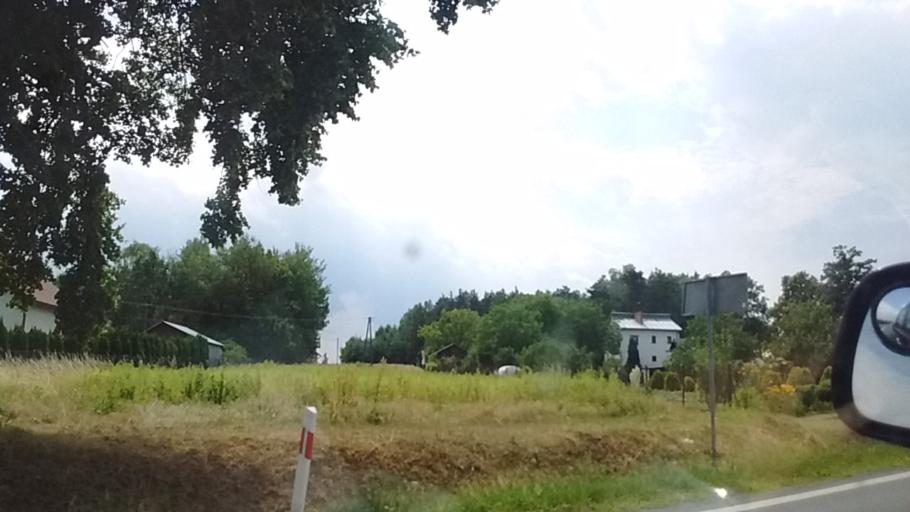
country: PL
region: Subcarpathian Voivodeship
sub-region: Powiat lancucki
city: Zolynia
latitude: 50.1888
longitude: 22.3235
